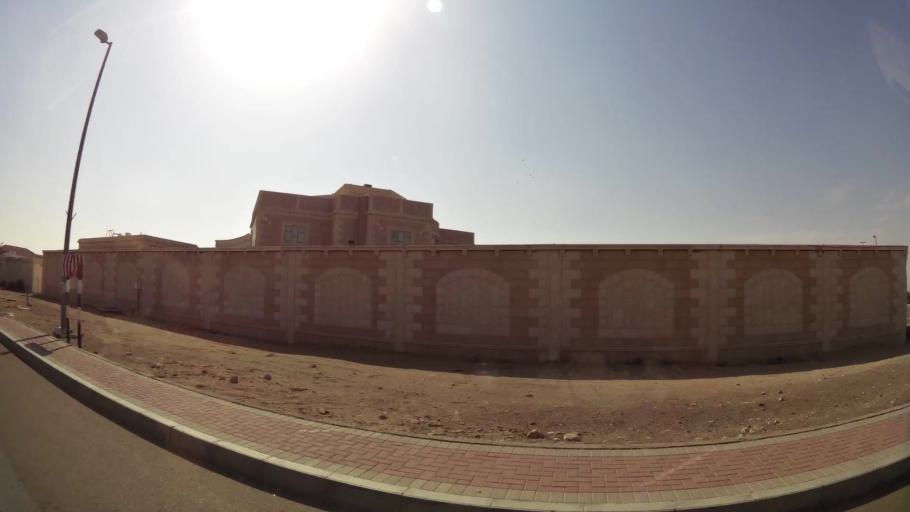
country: AE
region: Abu Dhabi
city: Al Ain
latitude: 24.0932
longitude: 55.9335
